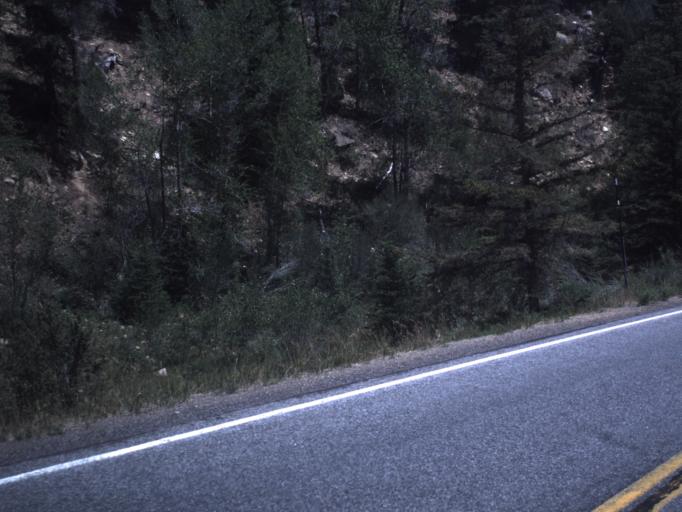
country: US
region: Utah
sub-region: Emery County
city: Huntington
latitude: 39.4647
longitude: -111.1468
